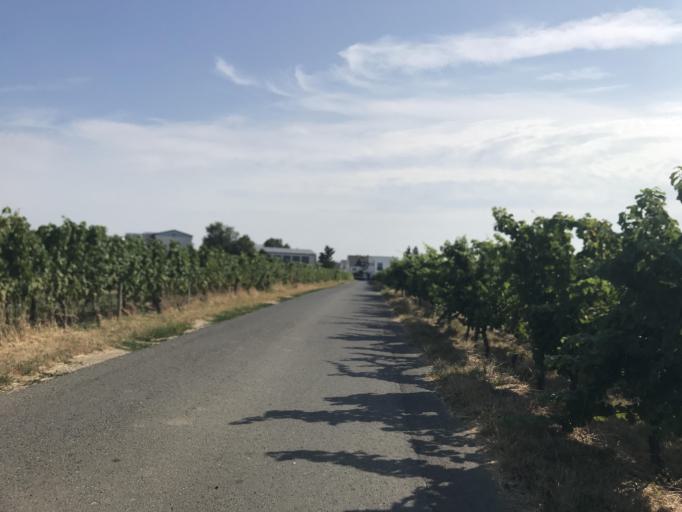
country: DE
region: Rheinland-Pfalz
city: Oestrich-Winkel
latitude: 50.0068
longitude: 8.0177
